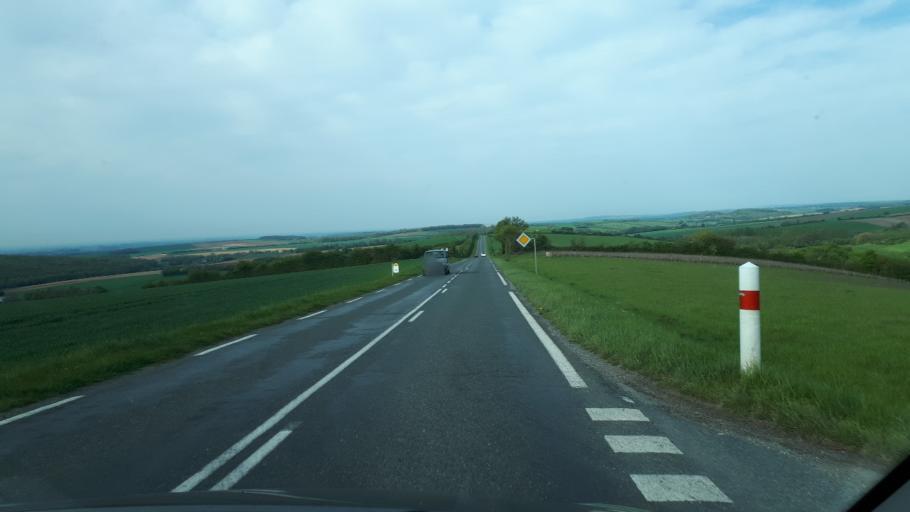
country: FR
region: Centre
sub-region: Departement du Cher
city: Rians
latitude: 47.2439
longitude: 2.6648
